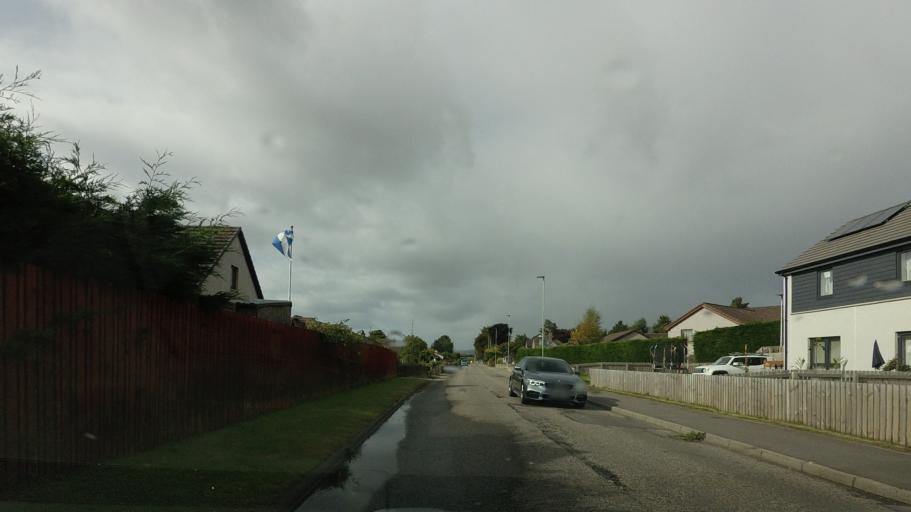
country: GB
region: Scotland
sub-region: Highland
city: Alness
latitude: 57.6969
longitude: -4.2416
